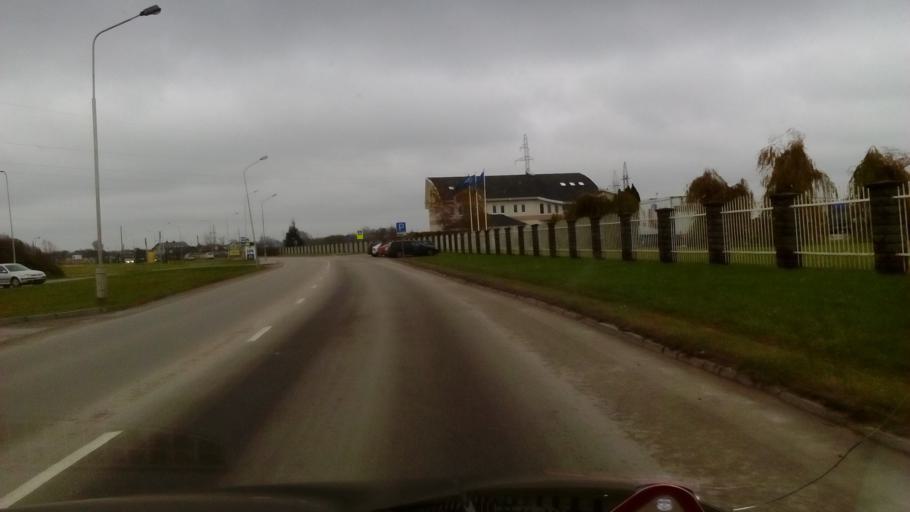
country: LT
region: Marijampoles apskritis
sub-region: Marijampole Municipality
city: Marijampole
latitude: 54.5304
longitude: 23.3582
